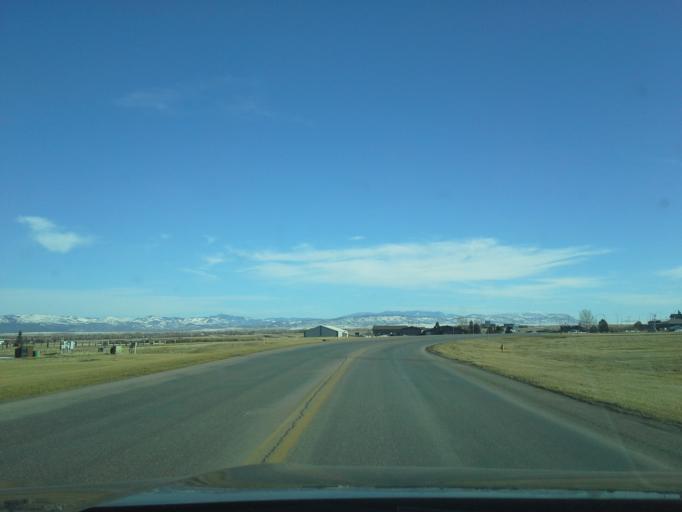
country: US
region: Montana
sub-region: Lewis and Clark County
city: Helena
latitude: 46.6132
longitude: -111.9969
